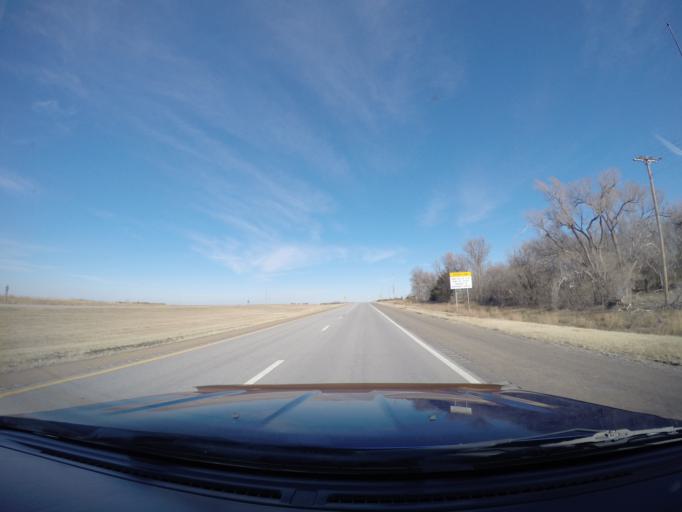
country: US
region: Kansas
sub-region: Republic County
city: Belleville
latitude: 39.8363
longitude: -97.6351
